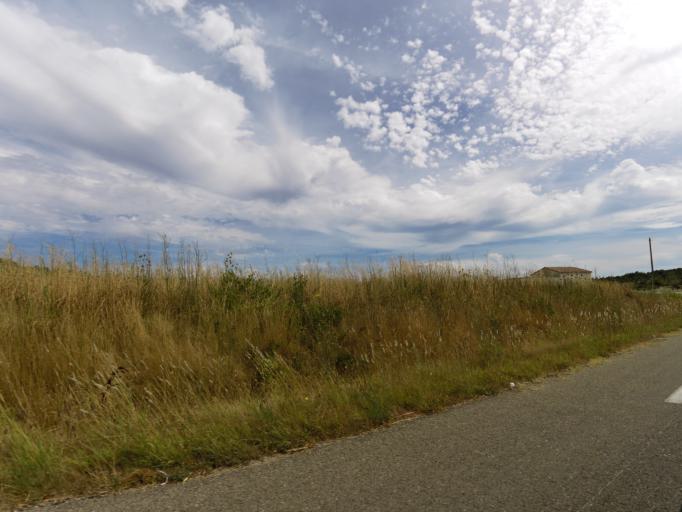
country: FR
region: Languedoc-Roussillon
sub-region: Departement du Gard
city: Villevieille
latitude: 43.8267
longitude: 4.1318
